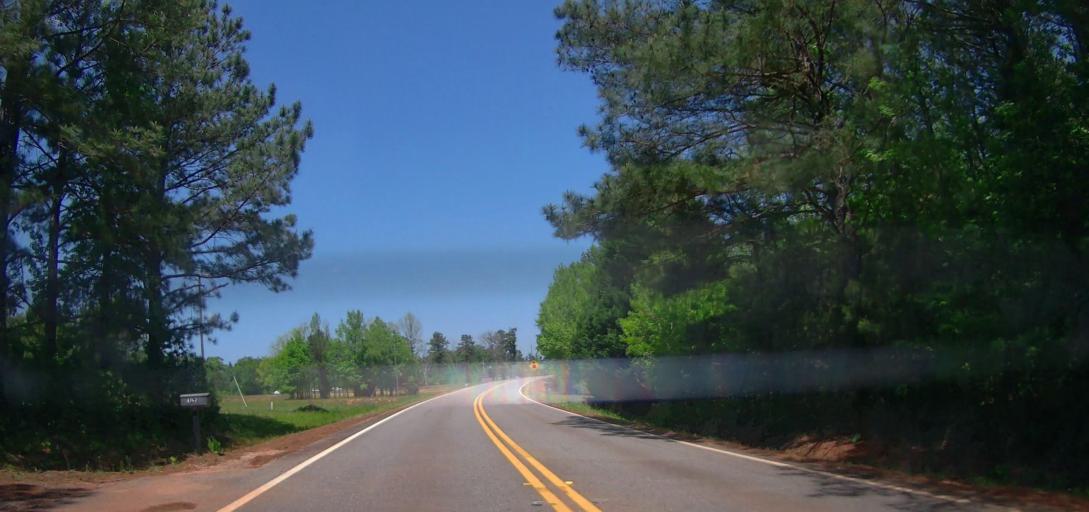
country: US
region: Georgia
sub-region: Jasper County
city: Monticello
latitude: 33.2904
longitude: -83.6452
